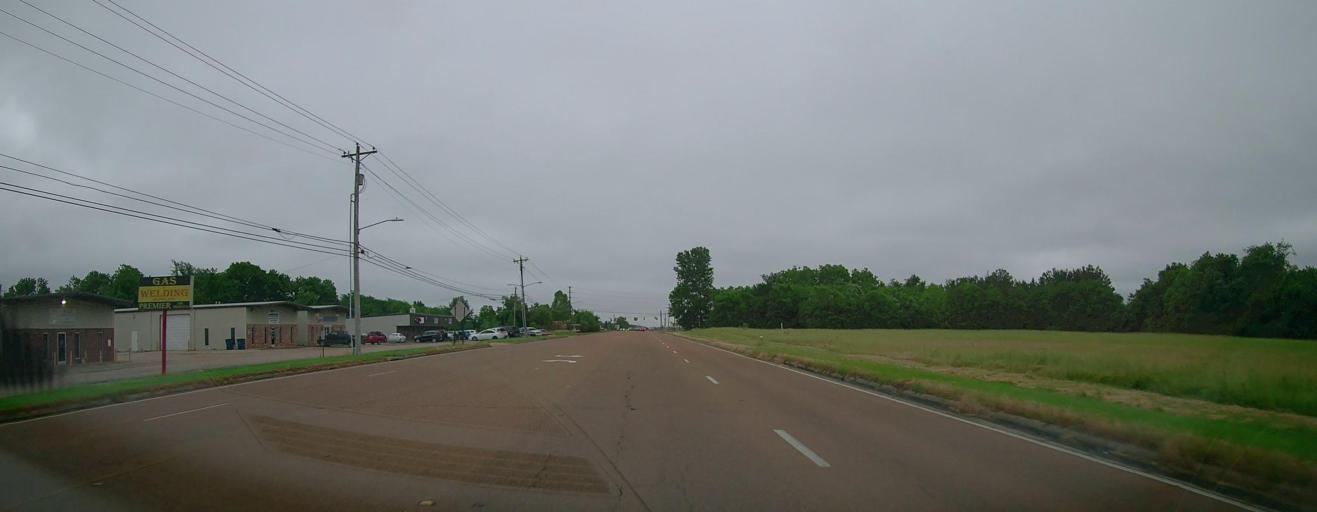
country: US
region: Mississippi
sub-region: De Soto County
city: Olive Branch
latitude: 34.9362
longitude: -89.7950
